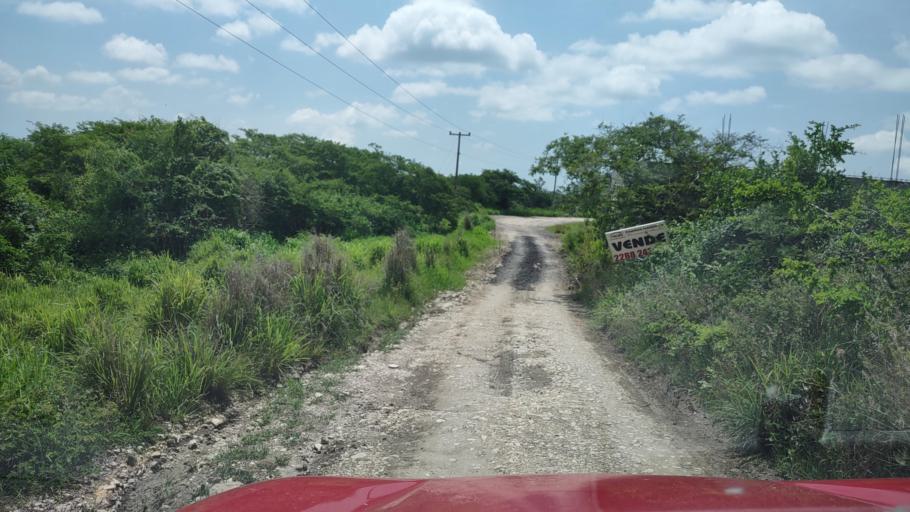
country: MX
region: Veracruz
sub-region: Emiliano Zapata
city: Dos Rios
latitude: 19.4634
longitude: -96.7925
